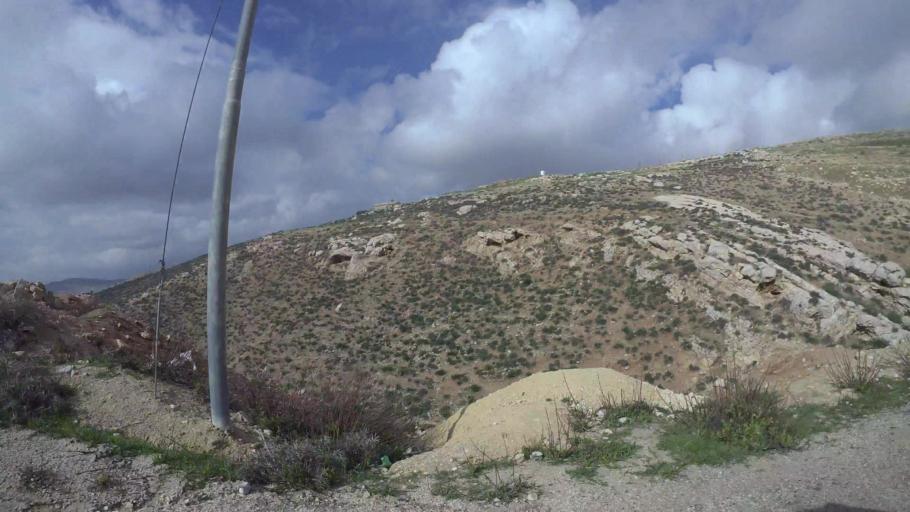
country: JO
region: Amman
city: Al Jubayhah
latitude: 32.0617
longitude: 35.8629
